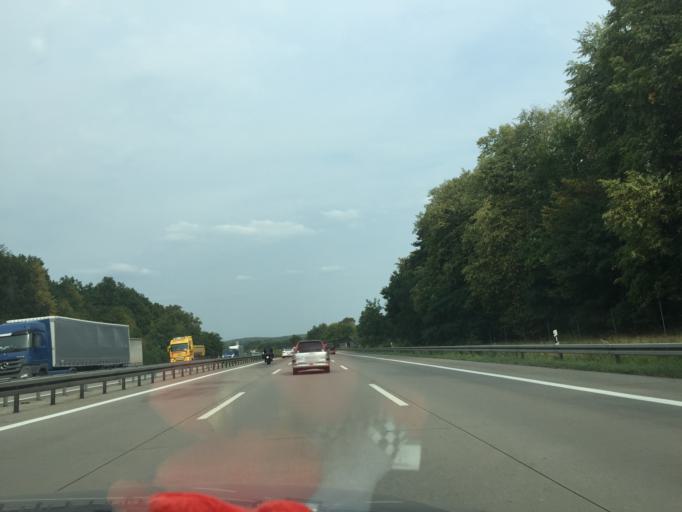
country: DE
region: Brandenburg
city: Wildau
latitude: 52.3103
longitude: 13.6242
